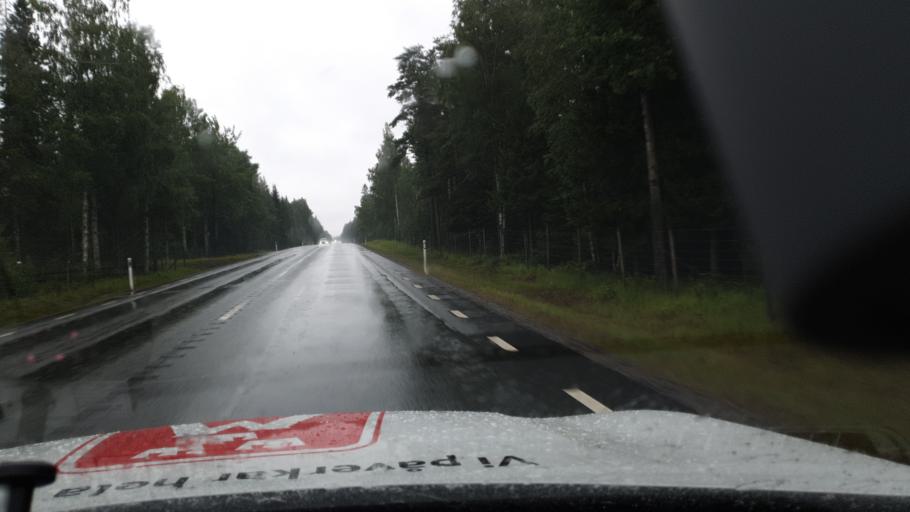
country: SE
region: Vaesterbotten
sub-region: Skelleftea Kommun
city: Burea
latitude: 64.5707
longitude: 21.2260
